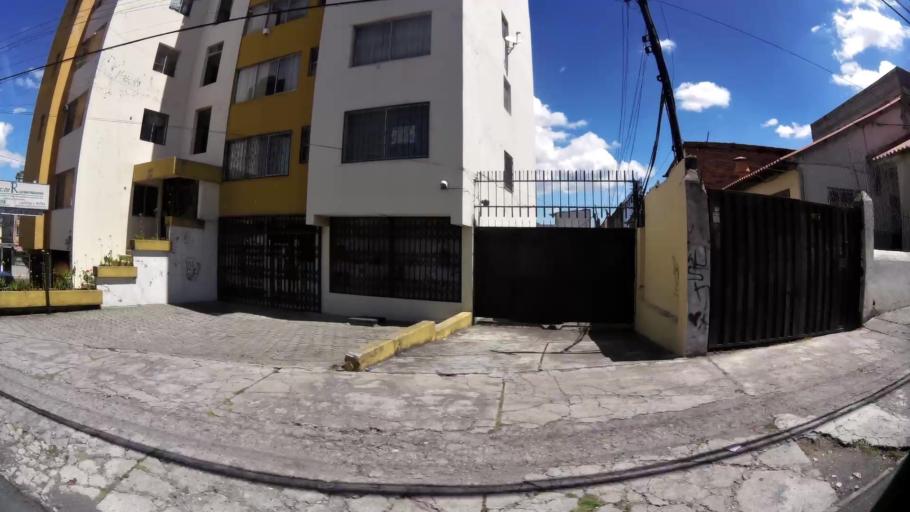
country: EC
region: Pichincha
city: Quito
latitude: -0.1252
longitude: -78.4808
